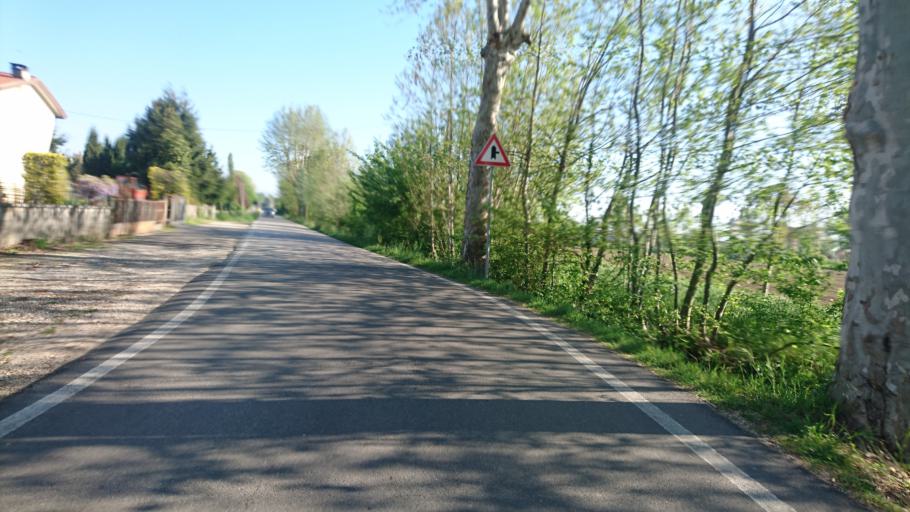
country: IT
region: Veneto
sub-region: Provincia di Padova
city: Massanzago-Ca' Baglioni-San Dono
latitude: 45.5500
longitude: 12.0027
